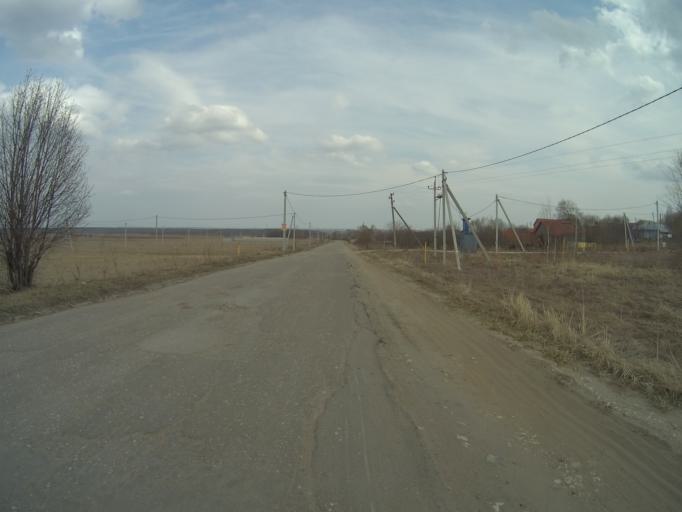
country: RU
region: Vladimir
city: Raduzhnyy
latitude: 56.0173
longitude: 40.3417
